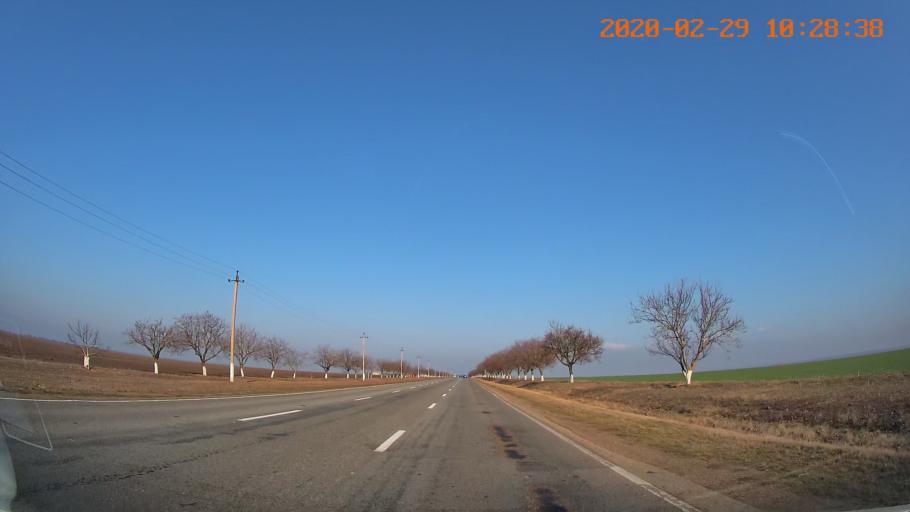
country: MD
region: Telenesti
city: Tiraspolul Nou
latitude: 46.9133
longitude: 29.5902
